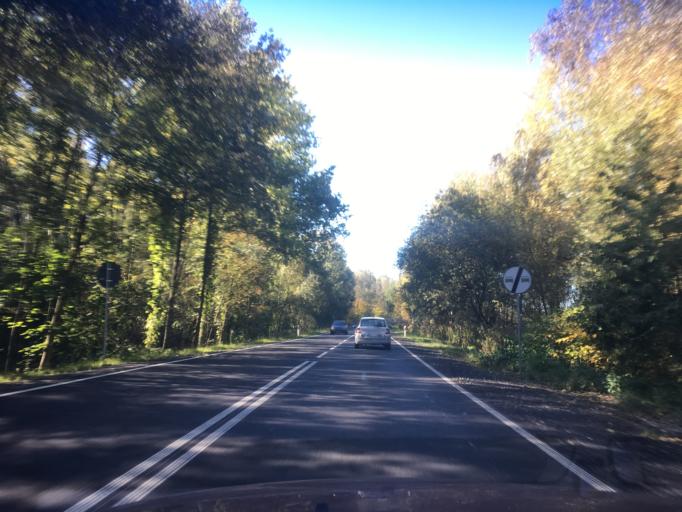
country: DE
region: Saxony
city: Hirschfelde
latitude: 50.9336
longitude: 14.8896
